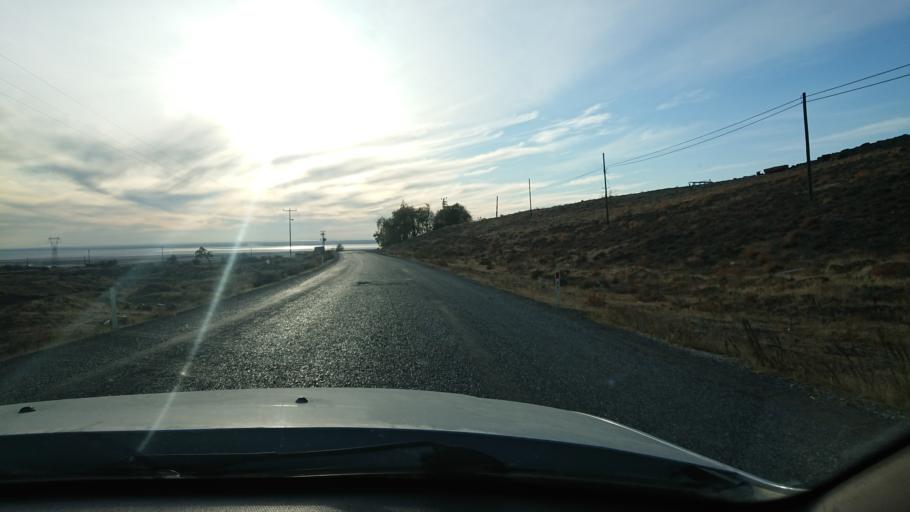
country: TR
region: Ankara
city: Sereflikochisar
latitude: 38.7459
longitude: 33.6822
